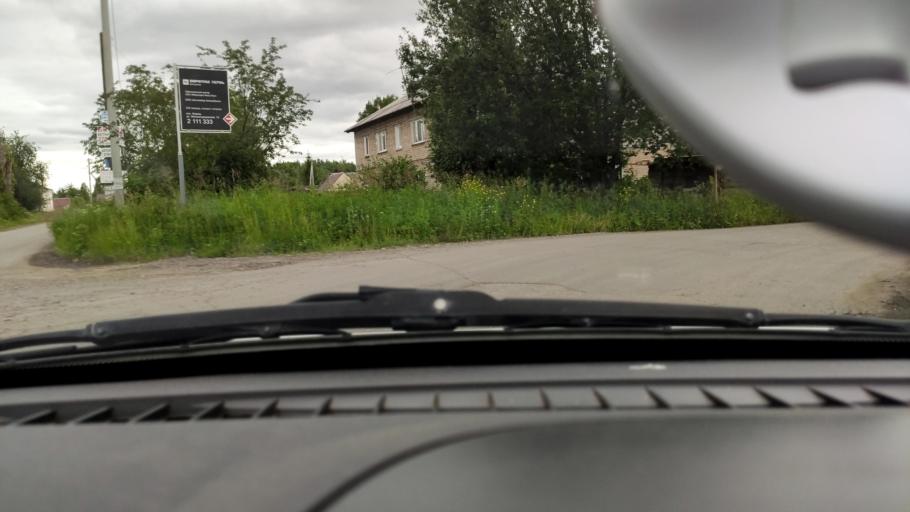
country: RU
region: Perm
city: Ferma
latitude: 57.8946
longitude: 56.2981
